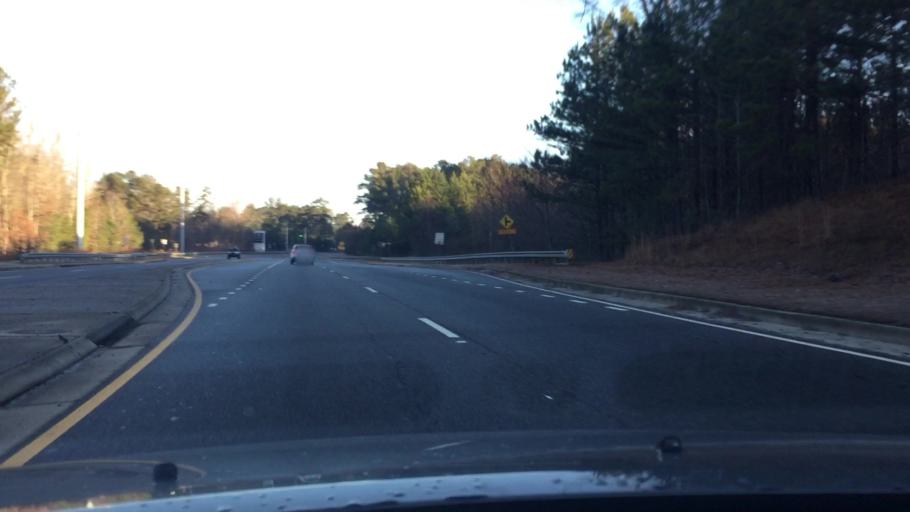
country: US
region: Georgia
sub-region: Forsyth County
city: Cumming
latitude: 34.1754
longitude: -84.1371
